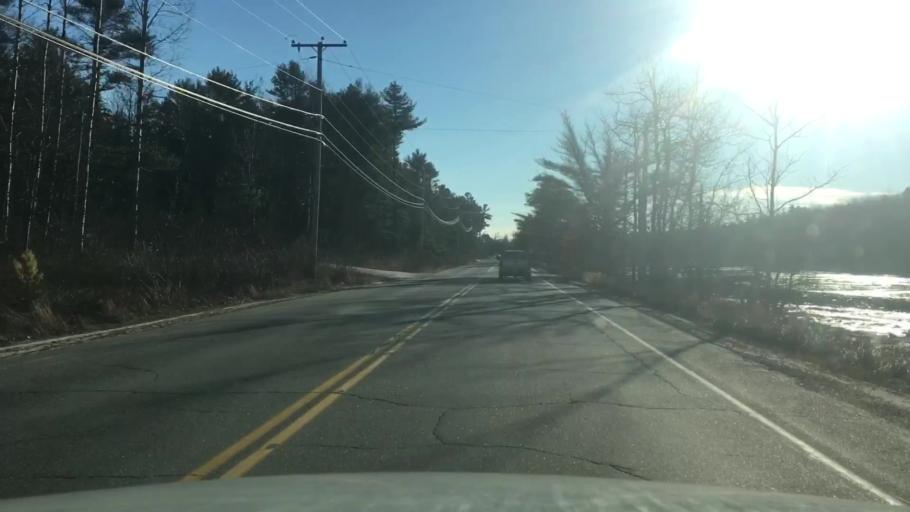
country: US
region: Maine
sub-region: Cumberland County
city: Brunswick
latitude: 43.8729
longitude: -69.9130
